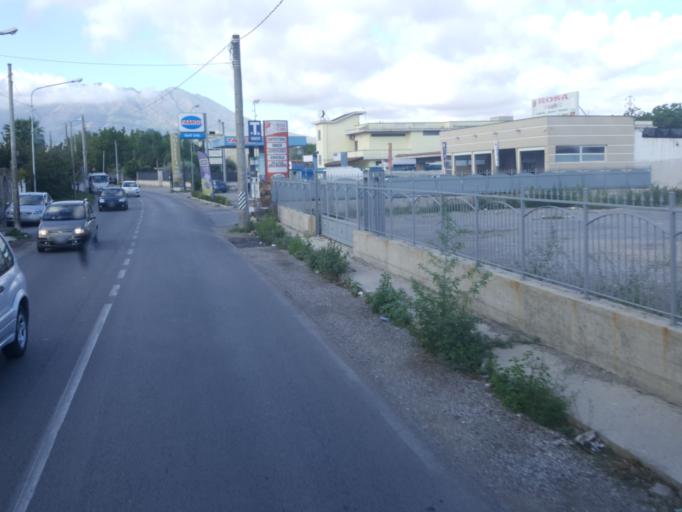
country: IT
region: Campania
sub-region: Provincia di Napoli
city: Piazzolla
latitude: 40.8877
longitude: 14.5146
